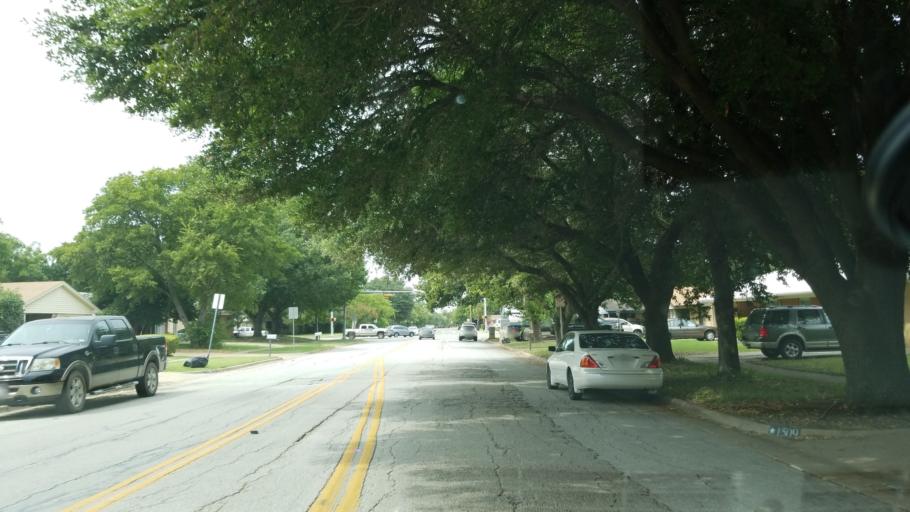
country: US
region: Texas
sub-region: Tarrant County
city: Arlington
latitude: 32.7200
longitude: -97.0834
